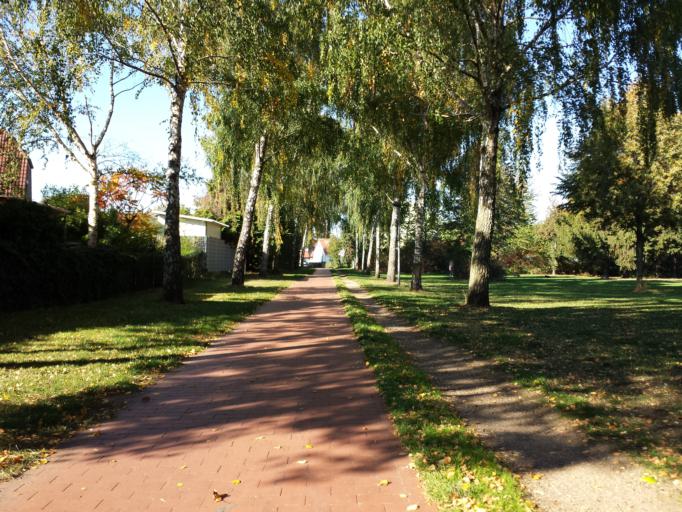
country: DE
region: Lower Saxony
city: Ritterhude
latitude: 53.1368
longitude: 8.7334
